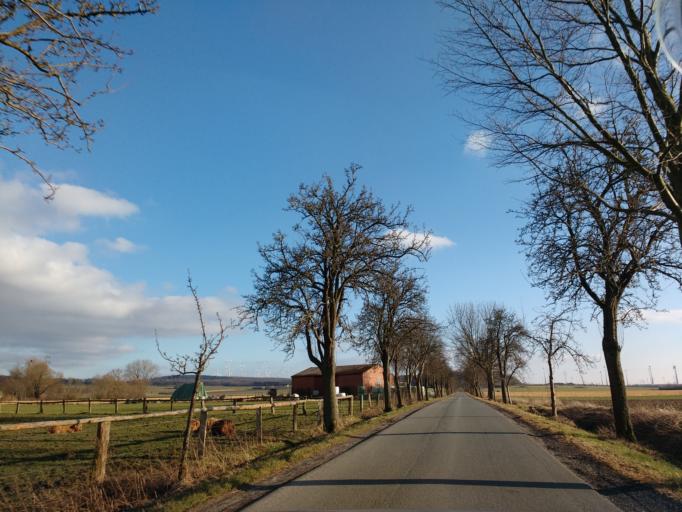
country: DE
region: North Rhine-Westphalia
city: Bad Lippspringe
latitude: 51.7679
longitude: 8.8384
